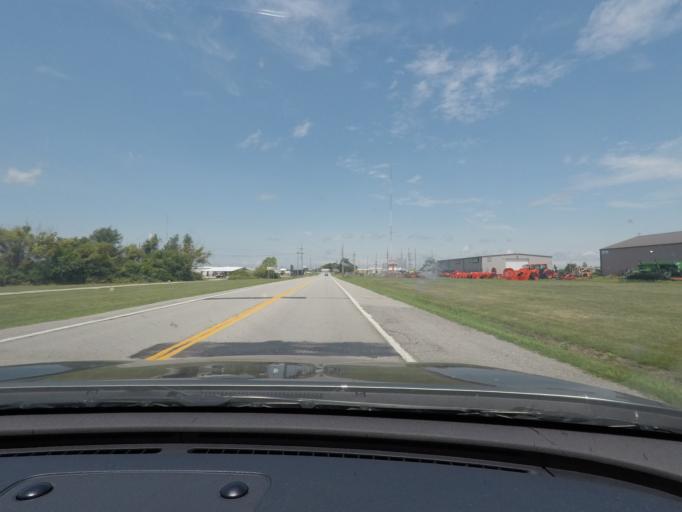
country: US
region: Missouri
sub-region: Saline County
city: Marshall
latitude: 39.1315
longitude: -93.2205
